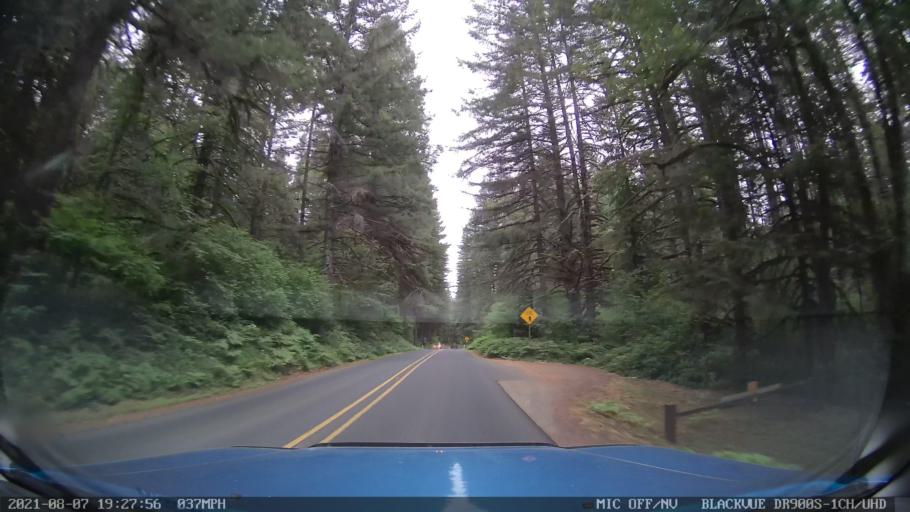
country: US
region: Oregon
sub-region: Linn County
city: Lyons
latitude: 44.8804
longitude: -122.6414
